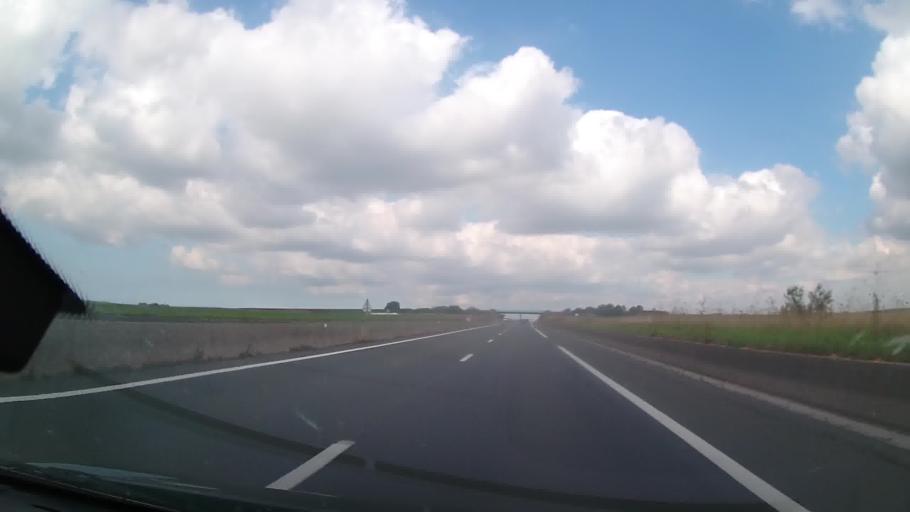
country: FR
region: Picardie
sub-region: Departement de la Somme
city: Rue
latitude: 50.3051
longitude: 1.7247
